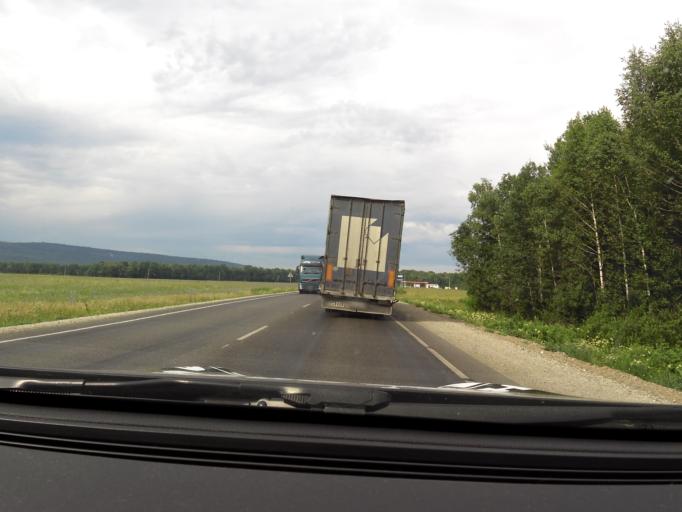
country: RU
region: Bashkortostan
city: Ulu-Telyak
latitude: 54.8553
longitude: 57.1364
